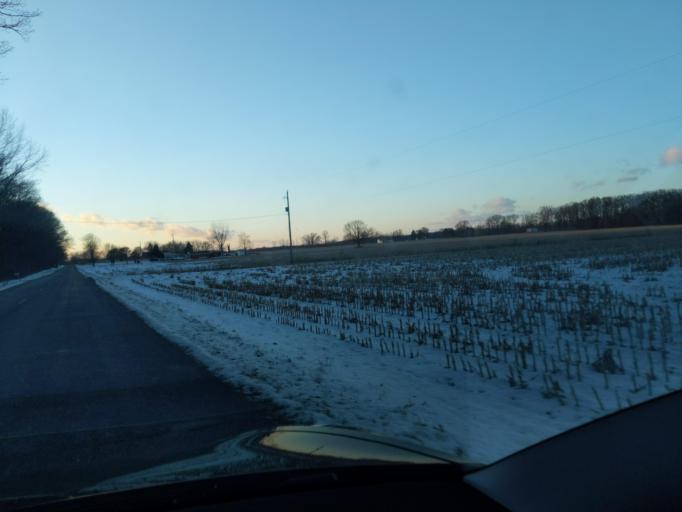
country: US
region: Michigan
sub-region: Ingham County
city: Stockbridge
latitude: 42.4537
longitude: -84.2697
